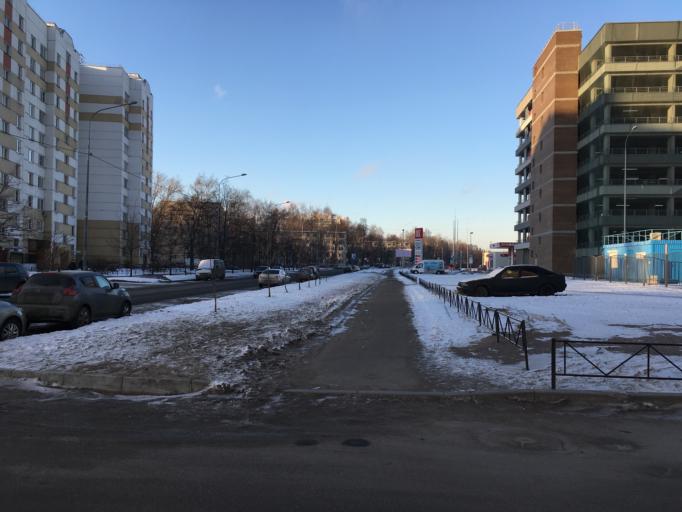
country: RU
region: St.-Petersburg
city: Krasnogvargeisky
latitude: 59.9769
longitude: 30.4357
